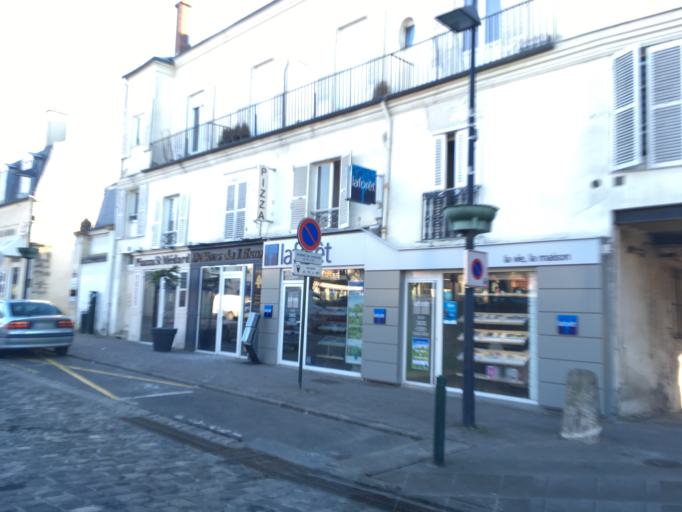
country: FR
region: Ile-de-France
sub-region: Departement de l'Essonne
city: Brunoy
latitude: 48.6981
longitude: 2.5019
